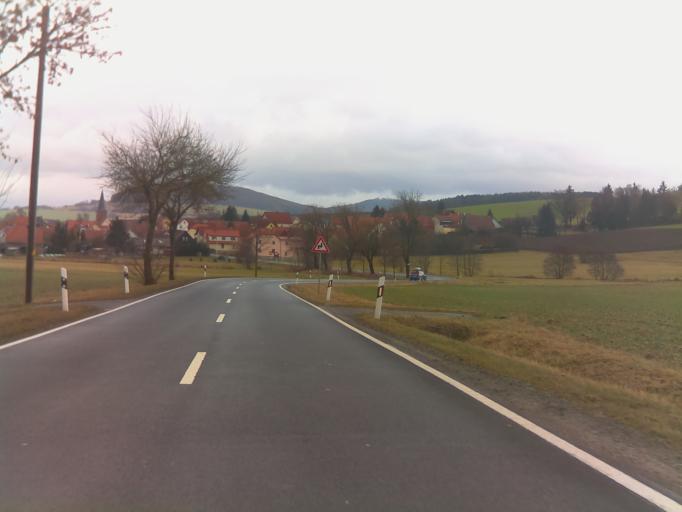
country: DE
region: Thuringia
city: Kaltenwestheim
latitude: 50.6081
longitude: 10.1241
